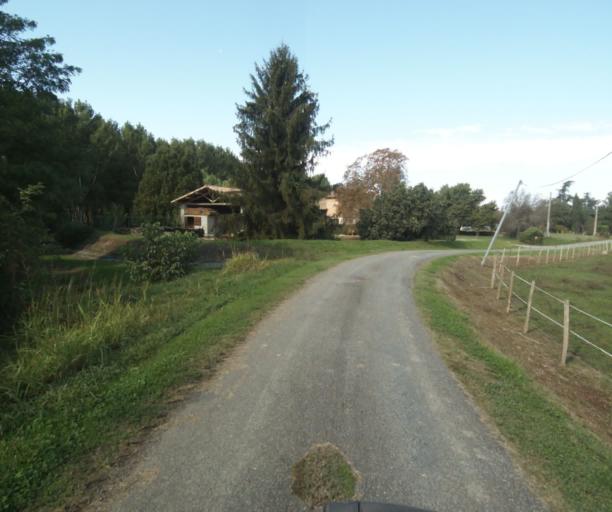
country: FR
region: Midi-Pyrenees
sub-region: Departement du Tarn-et-Garonne
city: Verdun-sur-Garonne
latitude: 43.8793
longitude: 1.2242
